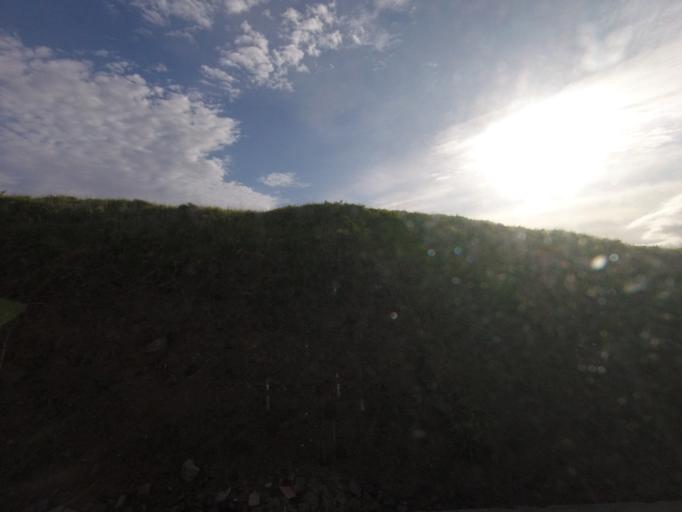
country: PT
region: Madeira
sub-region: Machico
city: Canical
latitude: 32.7474
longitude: -16.7400
